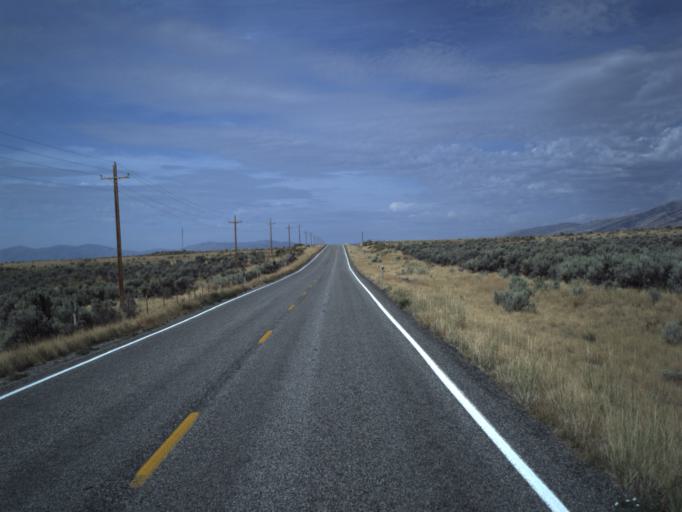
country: US
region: Idaho
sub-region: Cassia County
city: Burley
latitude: 41.8172
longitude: -113.2787
